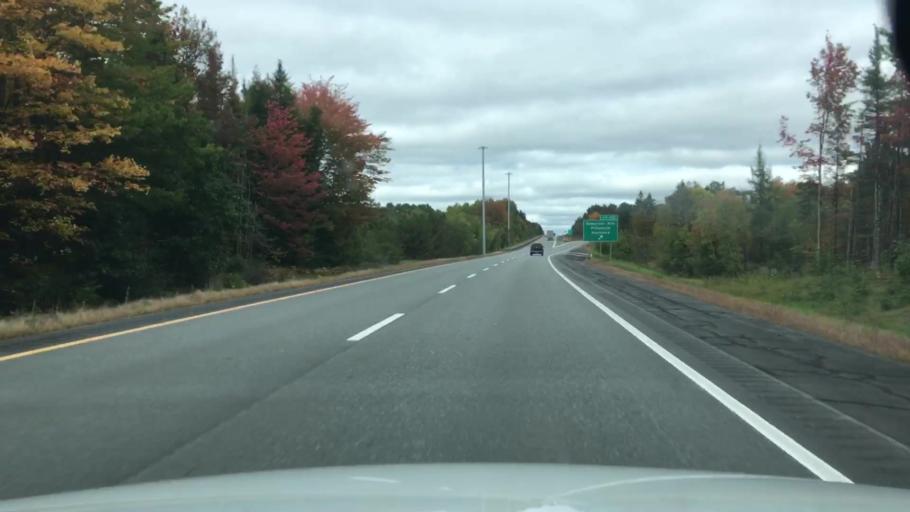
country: US
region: Maine
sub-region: Somerset County
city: Pittsfield
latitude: 44.7806
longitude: -69.4058
